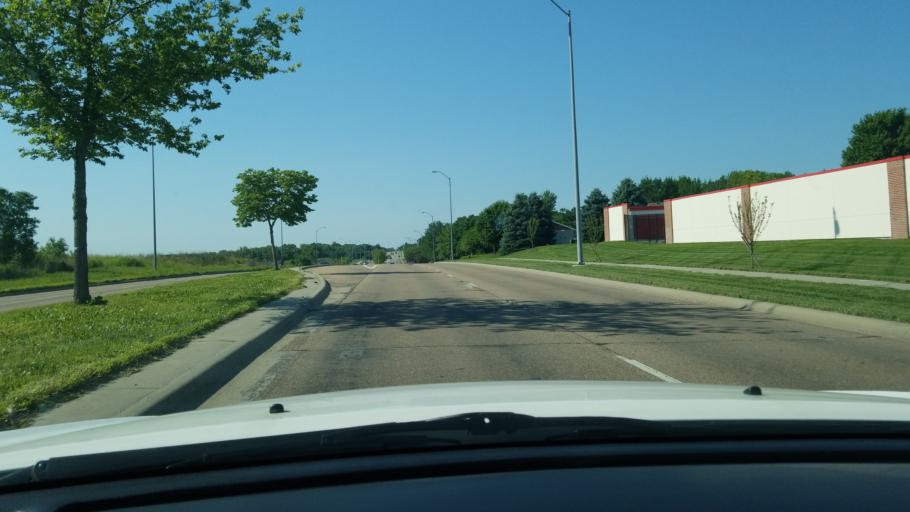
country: US
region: Nebraska
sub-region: Lancaster County
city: Lincoln
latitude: 40.7886
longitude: -96.6061
